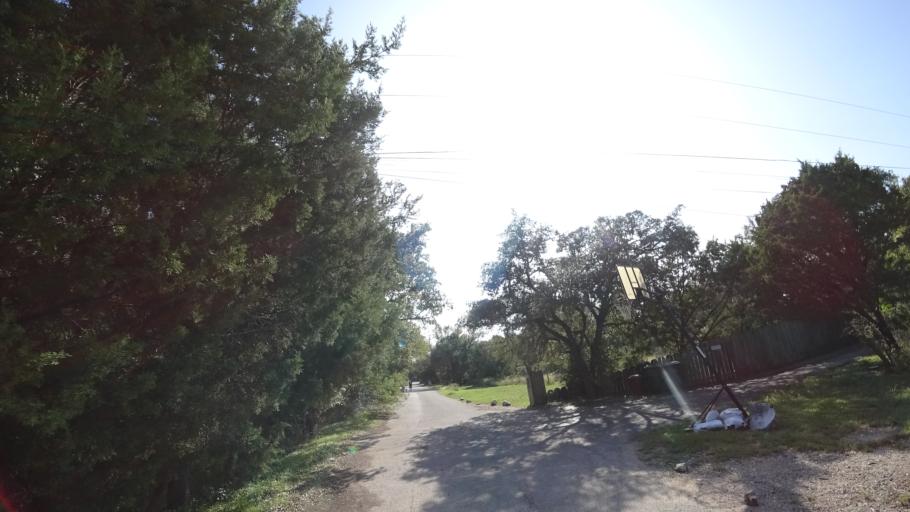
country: US
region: Texas
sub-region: Travis County
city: West Lake Hills
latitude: 30.2884
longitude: -97.7981
